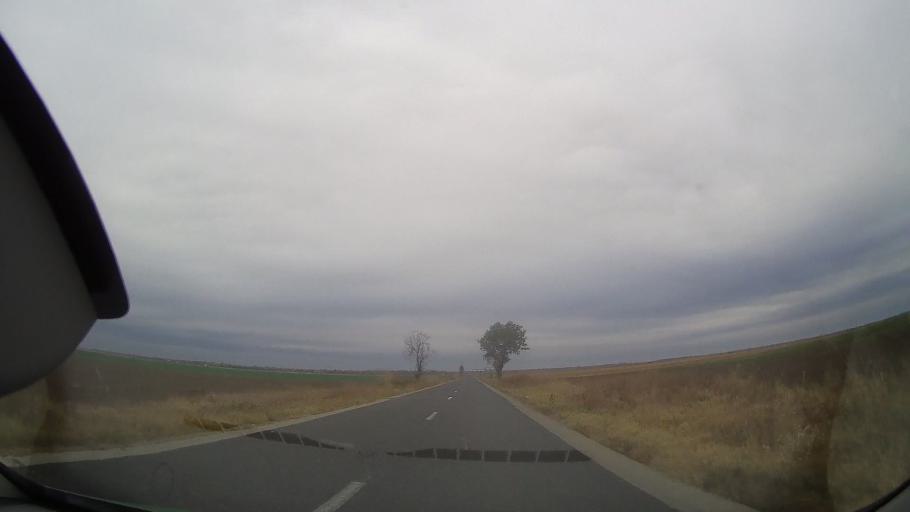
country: RO
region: Ialomita
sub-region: Comuna Milosesti
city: Milosesti
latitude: 44.7642
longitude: 27.1922
